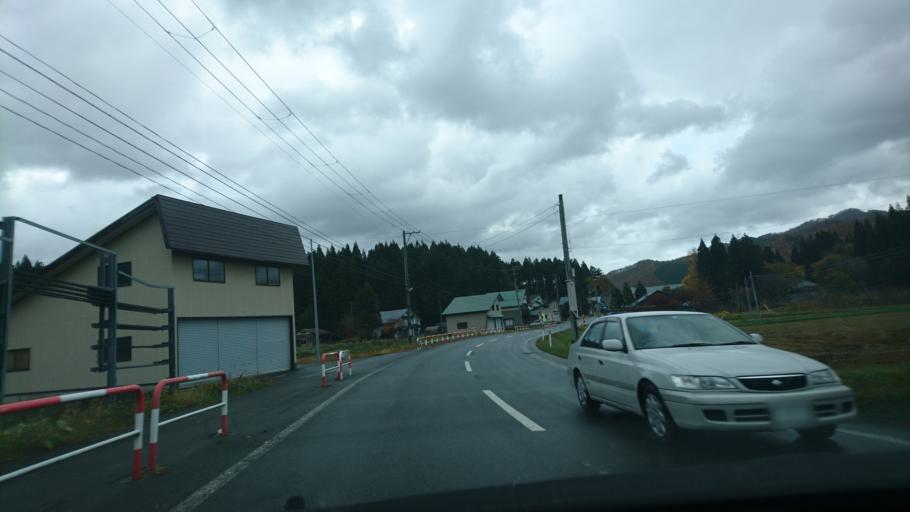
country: JP
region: Akita
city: Kakunodatemachi
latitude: 39.4756
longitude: 140.7860
